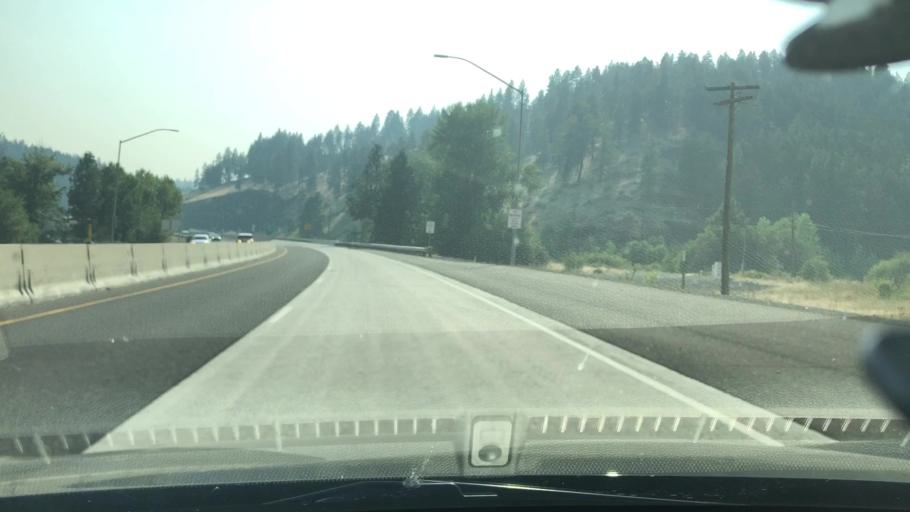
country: US
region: Oregon
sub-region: Union County
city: La Grande
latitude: 45.3477
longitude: -118.2209
